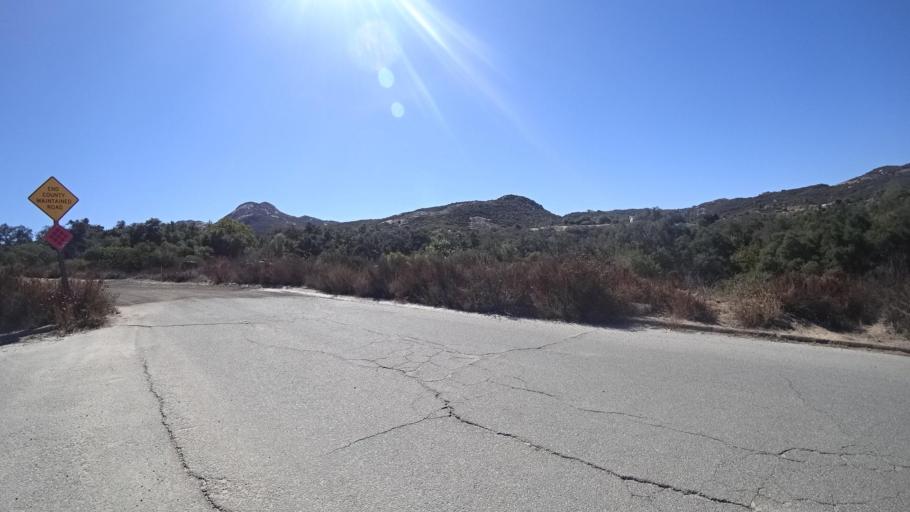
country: US
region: California
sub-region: San Diego County
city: Alpine
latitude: 32.7434
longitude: -116.7530
